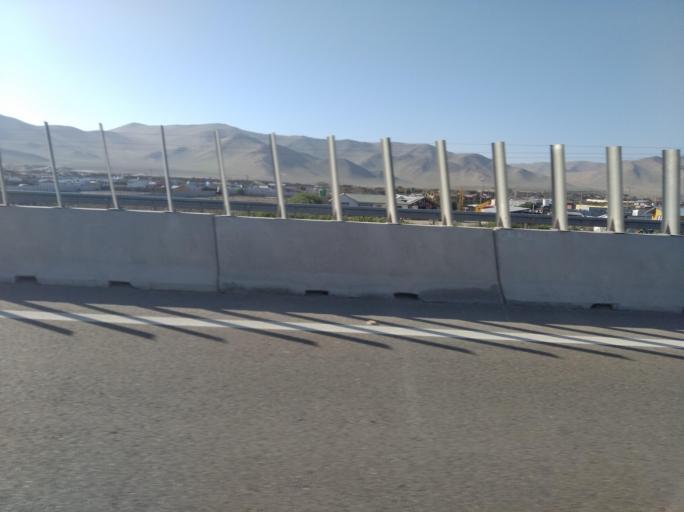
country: CL
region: Atacama
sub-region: Provincia de Copiapo
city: Copiapo
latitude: -27.3447
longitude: -70.6231
